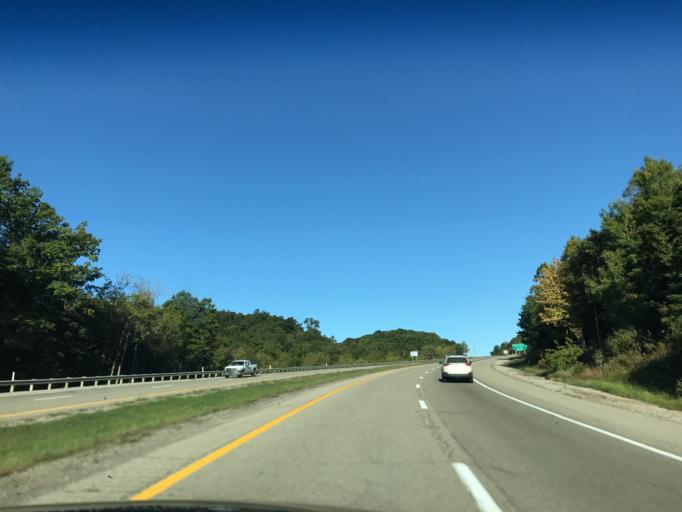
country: US
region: Ohio
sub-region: Washington County
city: Newport
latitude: 39.2504
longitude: -81.2607
